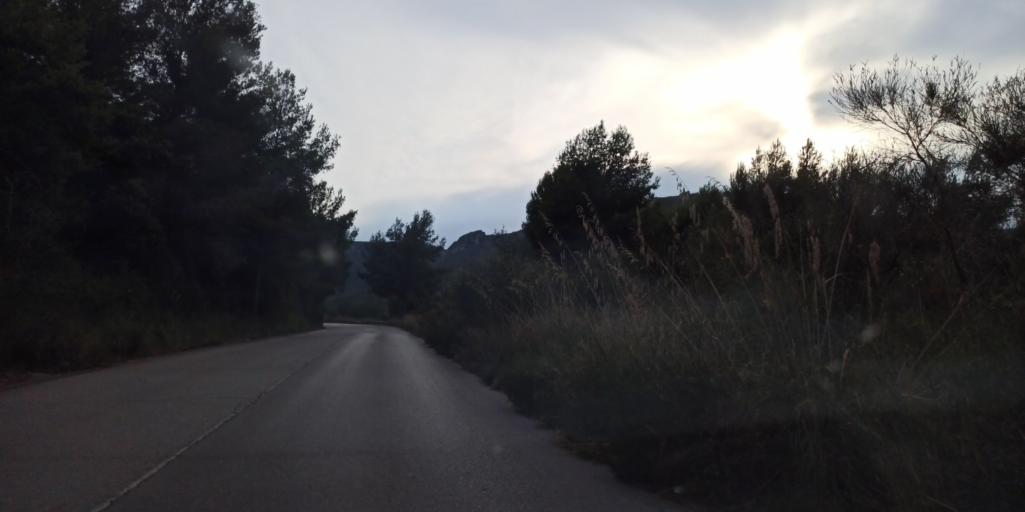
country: ES
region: Catalonia
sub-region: Provincia de Barcelona
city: Castelldefels
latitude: 41.2947
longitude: 1.9668
